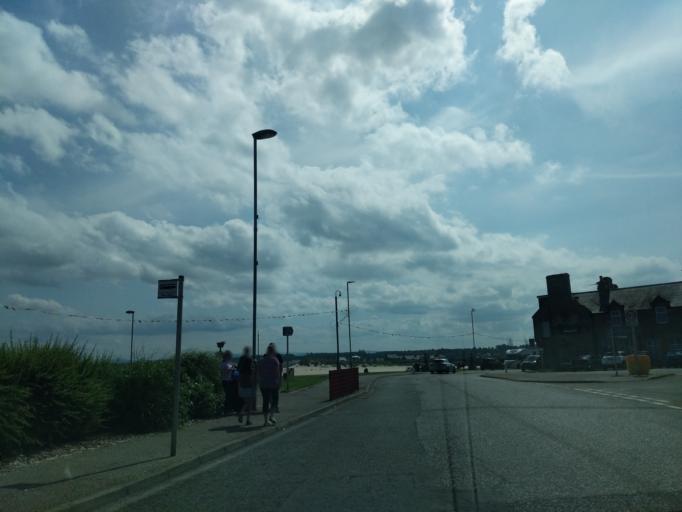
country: GB
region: Scotland
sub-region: Moray
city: Lossiemouth
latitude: 57.7206
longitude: -3.2805
